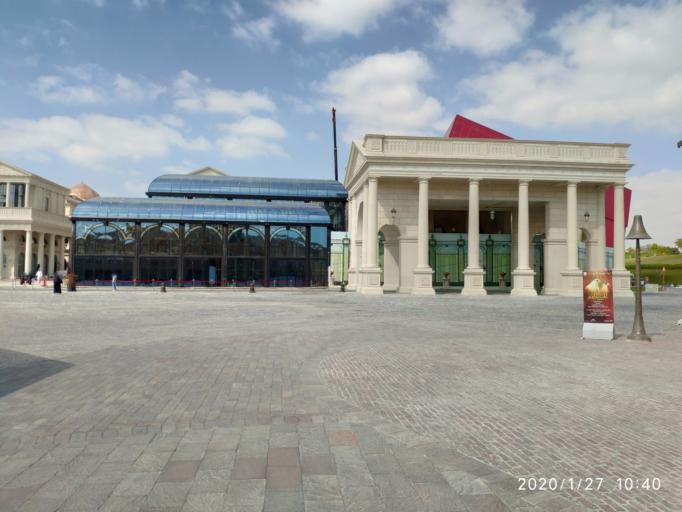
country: QA
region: Baladiyat ad Dawhah
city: Doha
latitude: 25.3610
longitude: 51.5250
